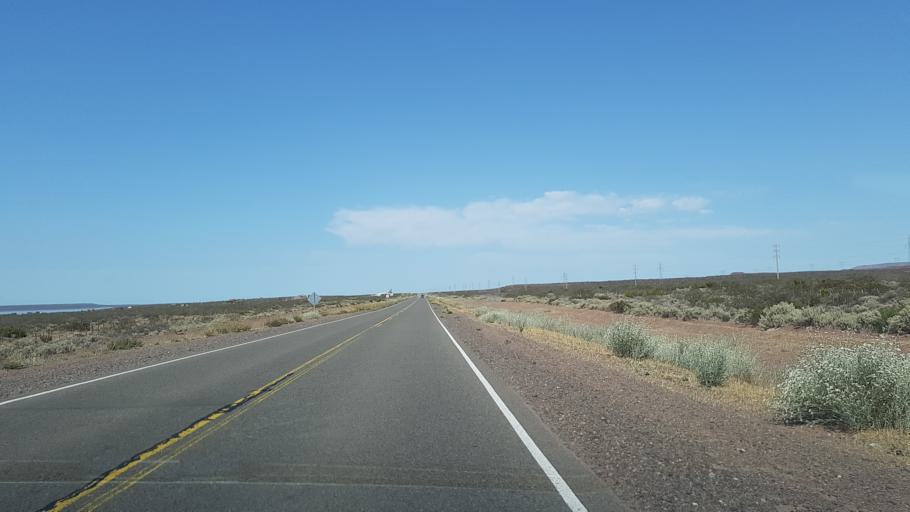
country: AR
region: Neuquen
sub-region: Departamento de Picun Leufu
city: Picun Leufu
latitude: -39.3265
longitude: -68.9608
